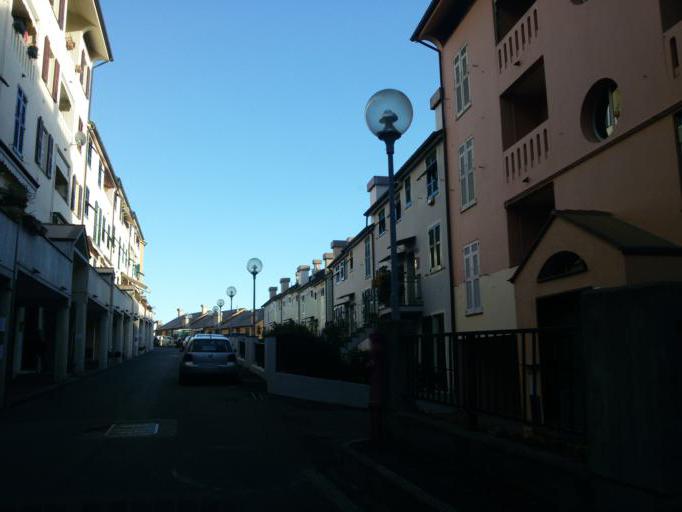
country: IT
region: Liguria
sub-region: Provincia di Genova
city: Bogliasco
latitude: 44.3924
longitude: 9.0131
